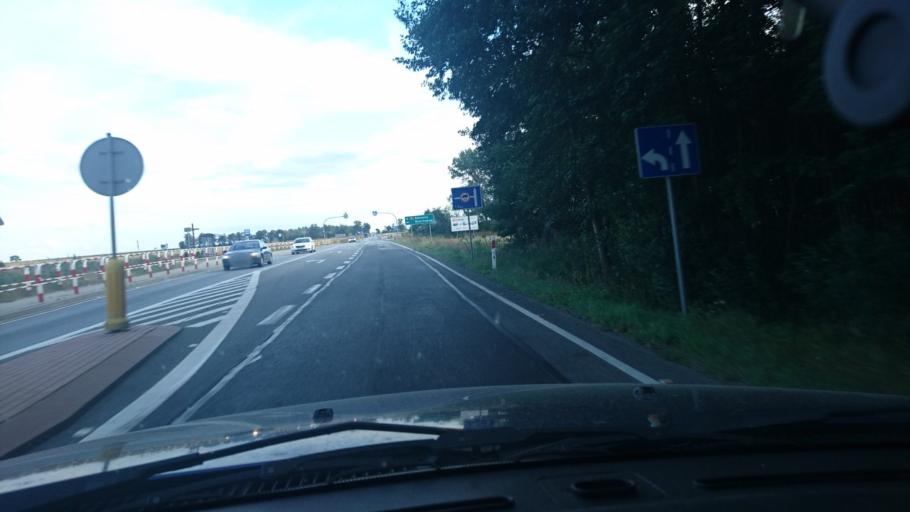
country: PL
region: Greater Poland Voivodeship
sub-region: Powiat kepinski
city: Opatow
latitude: 51.2054
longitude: 18.1474
